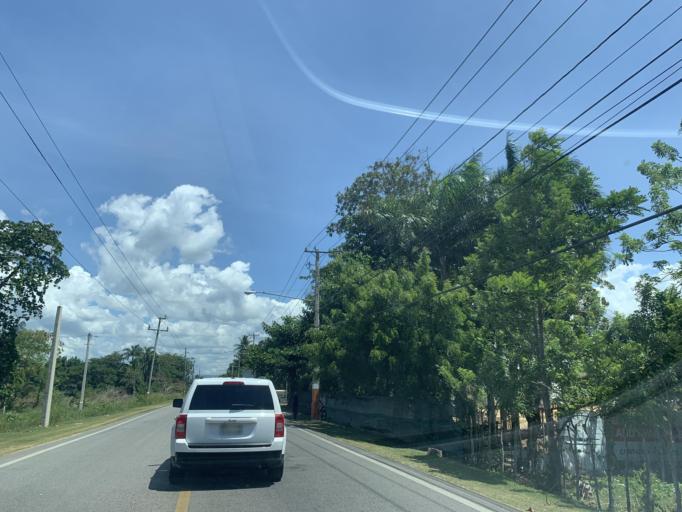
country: DO
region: Puerto Plata
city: Cabarete
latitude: 19.7287
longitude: -70.3881
